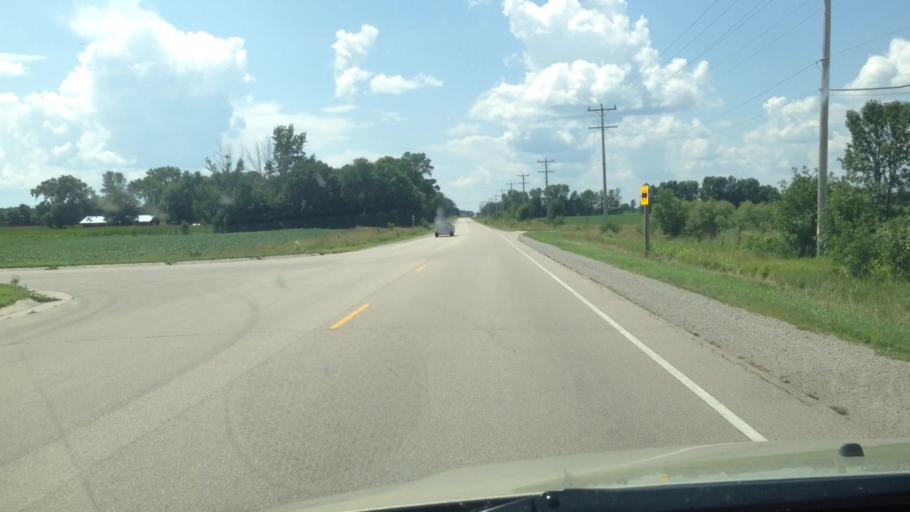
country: US
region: Wisconsin
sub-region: Brown County
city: Pulaski
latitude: 44.6734
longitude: -88.2810
